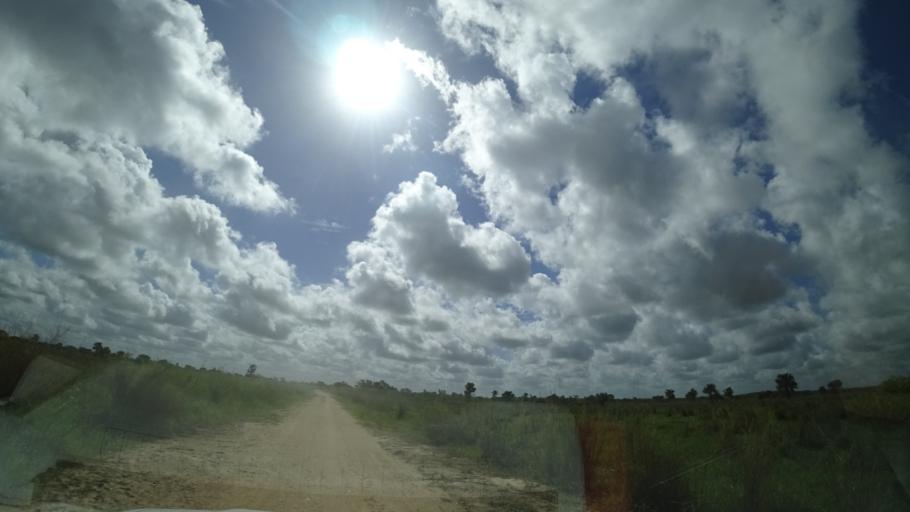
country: MZ
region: Sofala
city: Dondo
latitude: -19.3905
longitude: 34.5773
